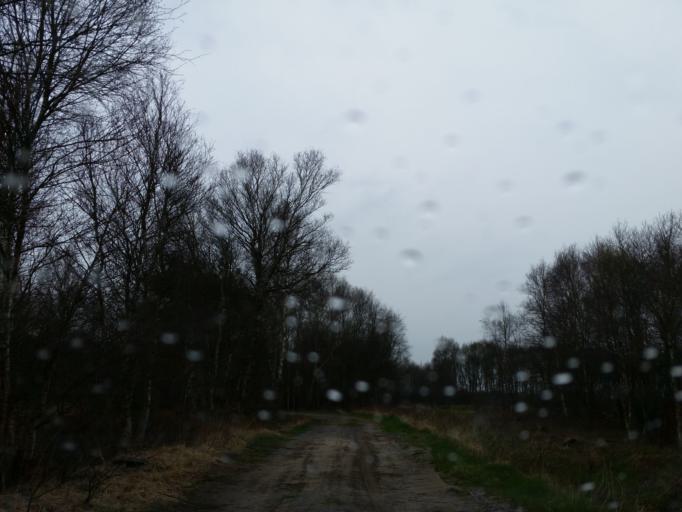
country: DE
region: Lower Saxony
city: Mittelstenahe
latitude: 53.6014
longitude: 9.0008
